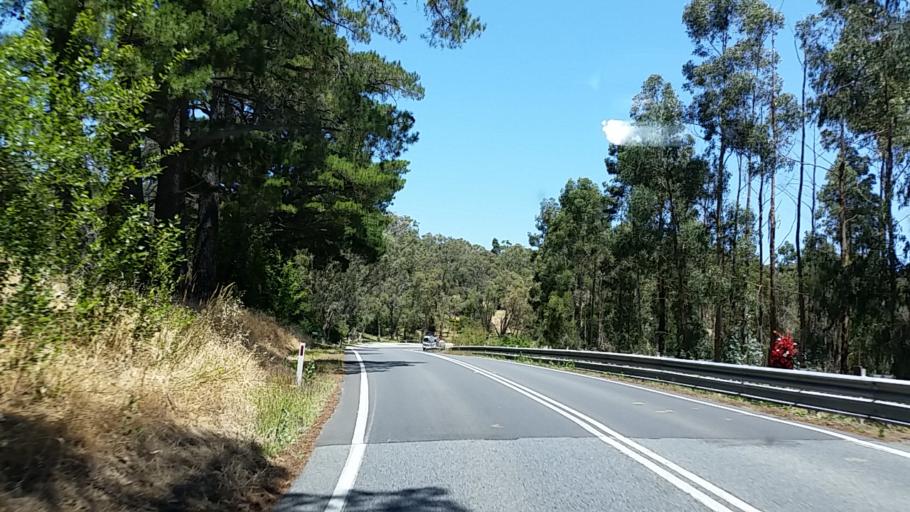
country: AU
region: South Australia
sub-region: Tea Tree Gully
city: Golden Grove
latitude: -34.8238
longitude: 138.7677
